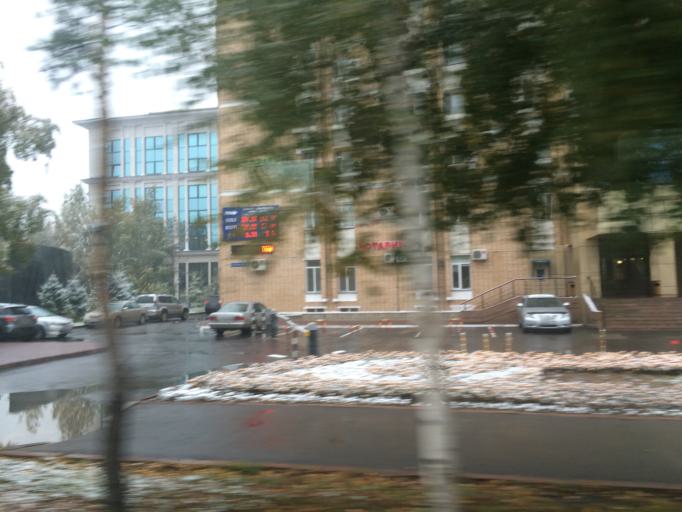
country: KZ
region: Astana Qalasy
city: Astana
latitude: 51.1692
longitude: 71.4260
